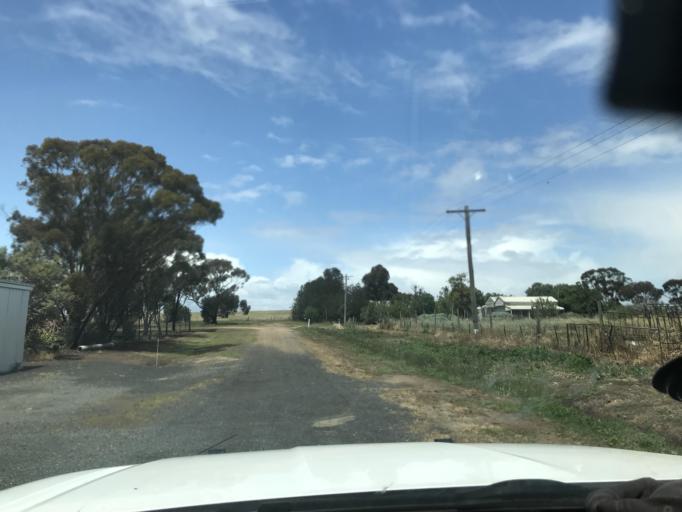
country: AU
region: South Australia
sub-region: Tatiara
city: Bordertown
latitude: -36.3621
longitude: 141.1240
